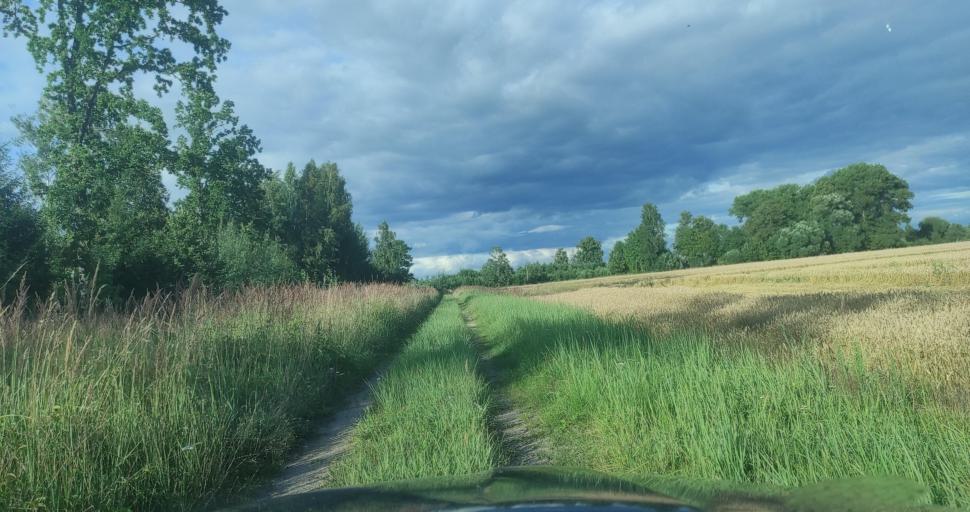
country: LV
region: Dobeles Rajons
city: Dobele
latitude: 56.7057
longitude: 23.4513
